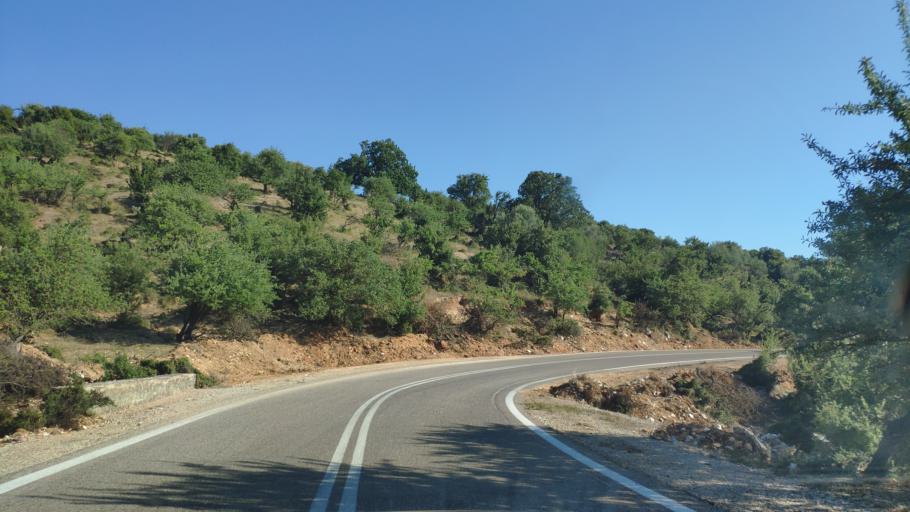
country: GR
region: West Greece
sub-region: Nomos Aitolias kai Akarnanias
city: Archontochorion
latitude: 38.6911
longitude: 21.0608
